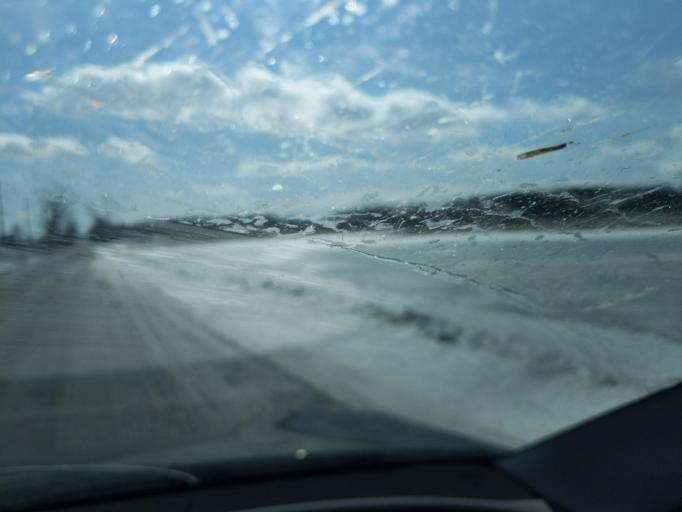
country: US
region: Michigan
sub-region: Livingston County
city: Fowlerville
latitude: 42.6051
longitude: -84.0906
